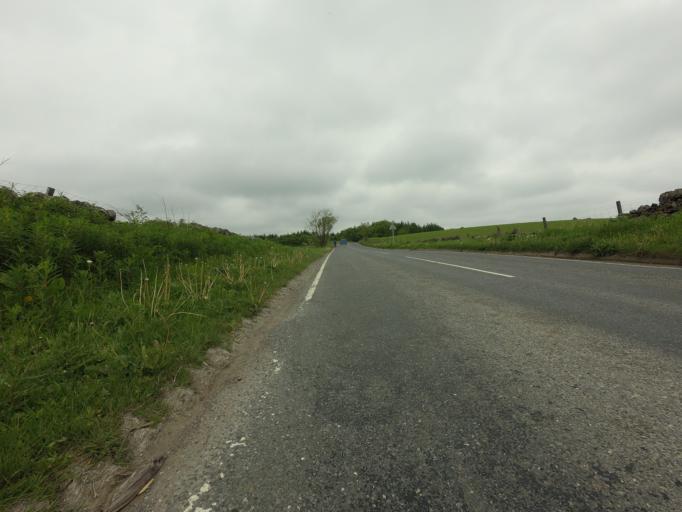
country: GB
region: Scotland
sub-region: Fife
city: Townhill
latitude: 56.1175
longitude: -3.4445
